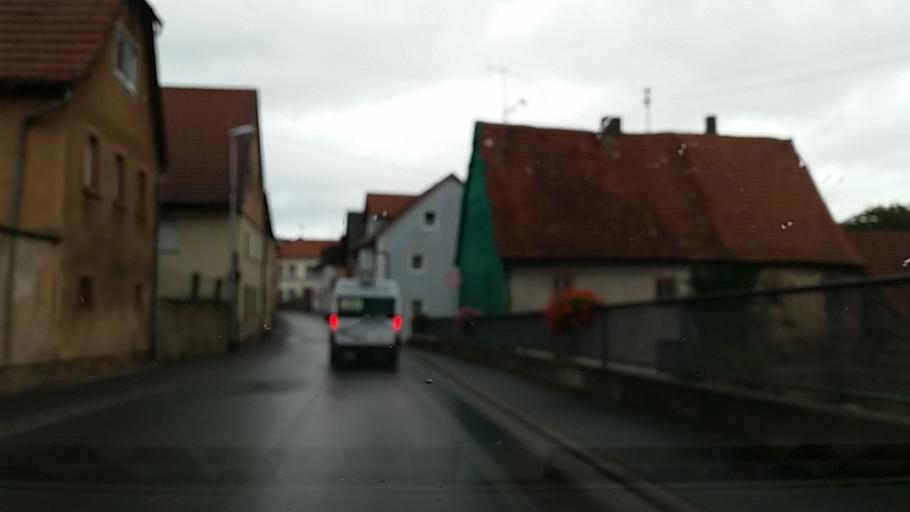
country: DE
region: Bavaria
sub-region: Regierungsbezirk Unterfranken
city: Gossenheim
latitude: 50.0020
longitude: 9.7545
